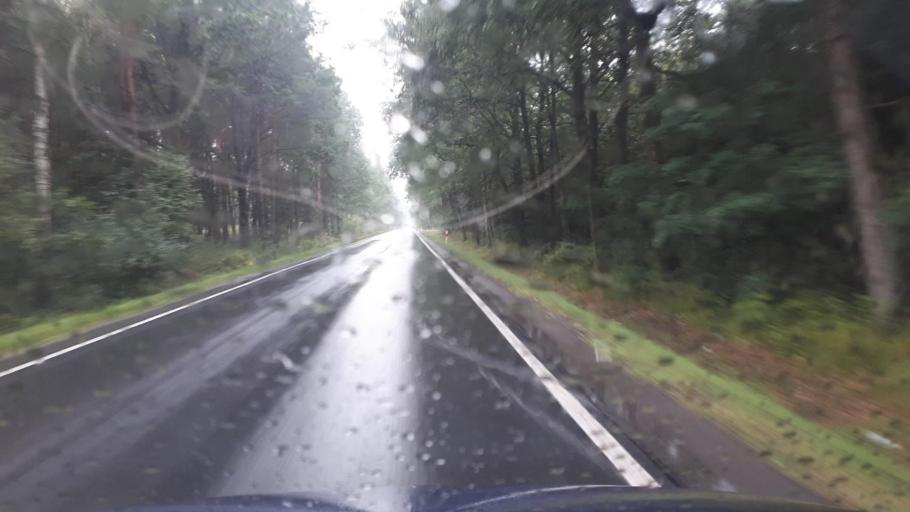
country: PL
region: Silesian Voivodeship
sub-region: Powiat tarnogorski
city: Tworog
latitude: 50.5300
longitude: 18.6826
